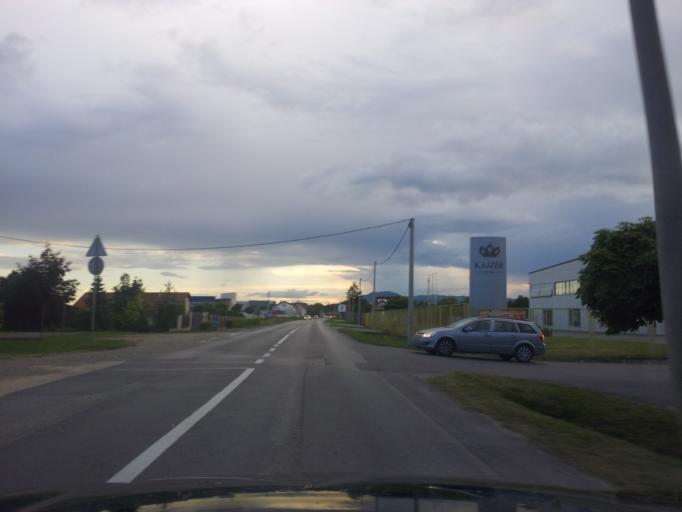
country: HR
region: Grad Zagreb
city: Lucko
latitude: 45.7595
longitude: 15.8680
